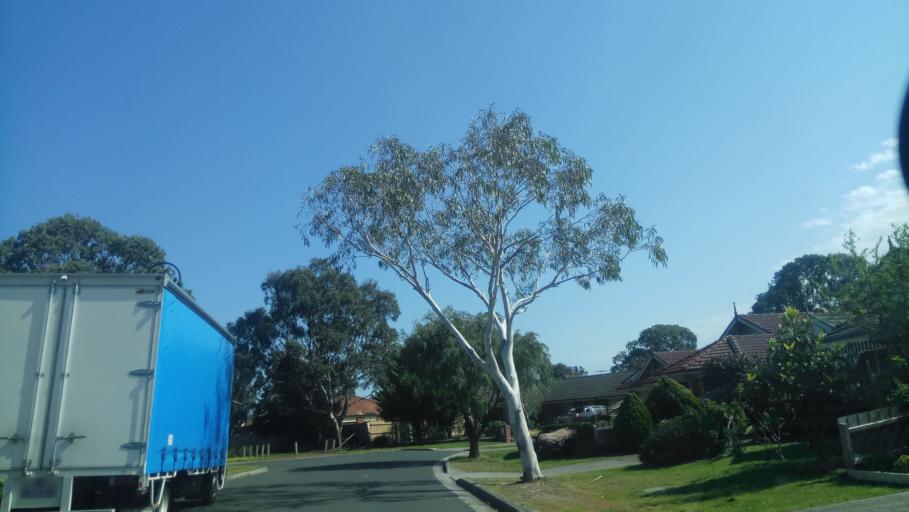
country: AU
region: Victoria
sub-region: Casey
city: Lynbrook
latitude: -38.0553
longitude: 145.2572
